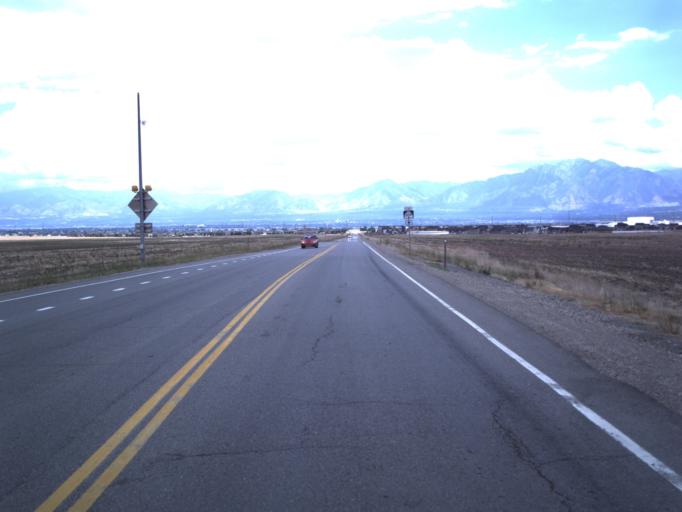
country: US
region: Utah
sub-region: Salt Lake County
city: Oquirrh
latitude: 40.5765
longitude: -112.0605
